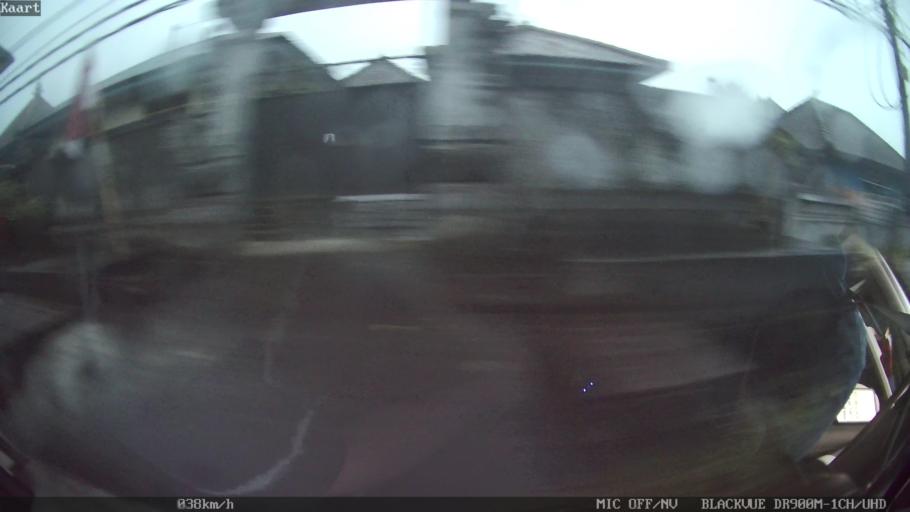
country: ID
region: Bali
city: Banjar Taro Kelod
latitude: -8.3223
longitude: 115.2954
